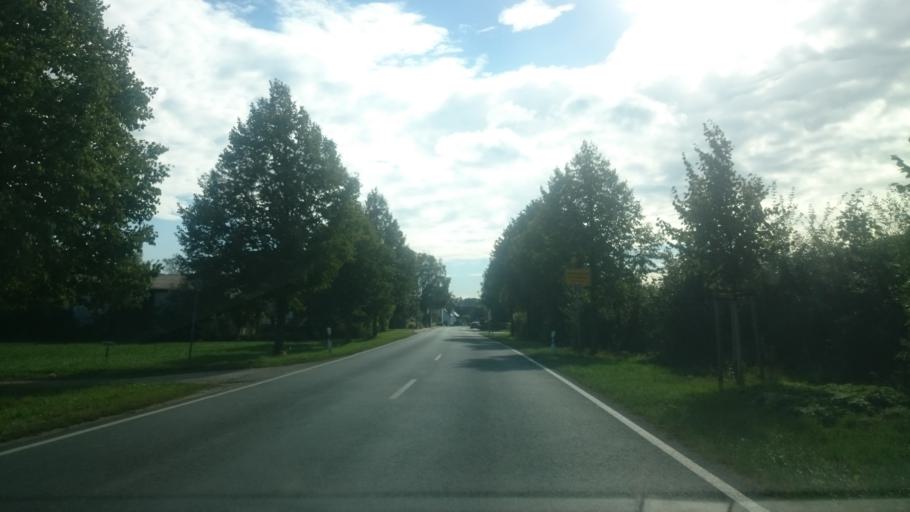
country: DE
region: Bavaria
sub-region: Regierungsbezirk Mittelfranken
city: Thalmassing
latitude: 49.1477
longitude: 11.2594
